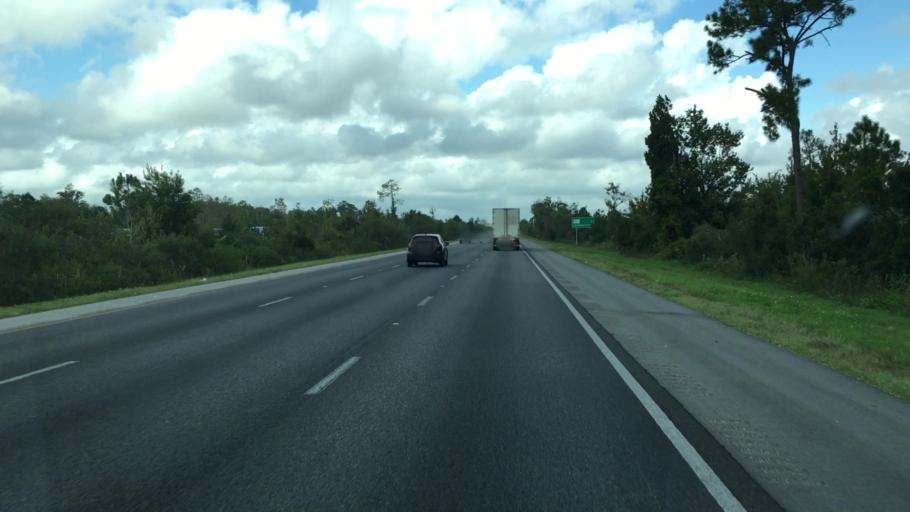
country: US
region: Florida
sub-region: Volusia County
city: Glencoe
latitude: 29.0245
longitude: -80.9952
